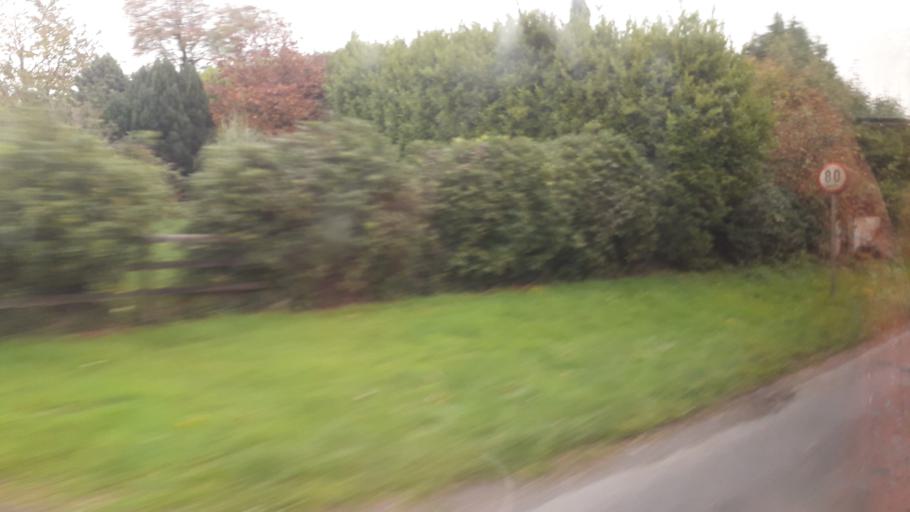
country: IE
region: Munster
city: Ballina
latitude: 52.7987
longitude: -8.4343
